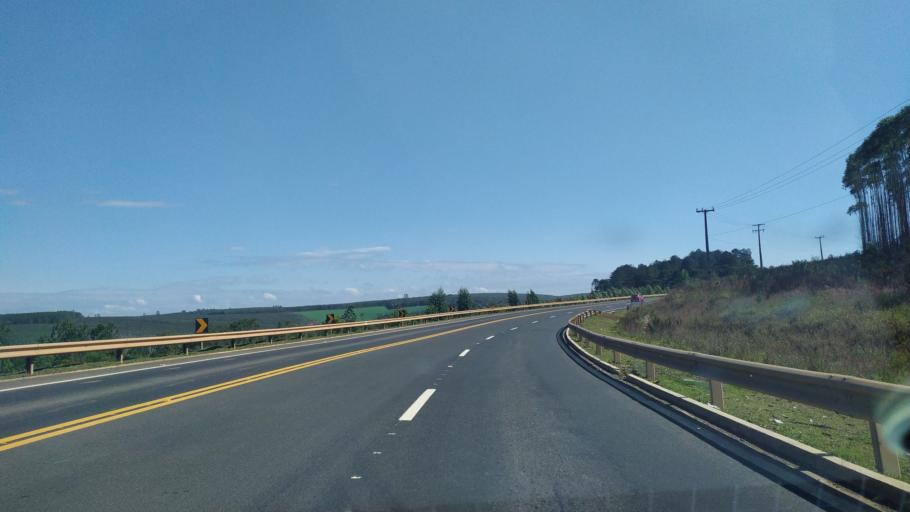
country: BR
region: Parana
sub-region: Telemaco Borba
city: Telemaco Borba
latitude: -24.2572
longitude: -50.7320
